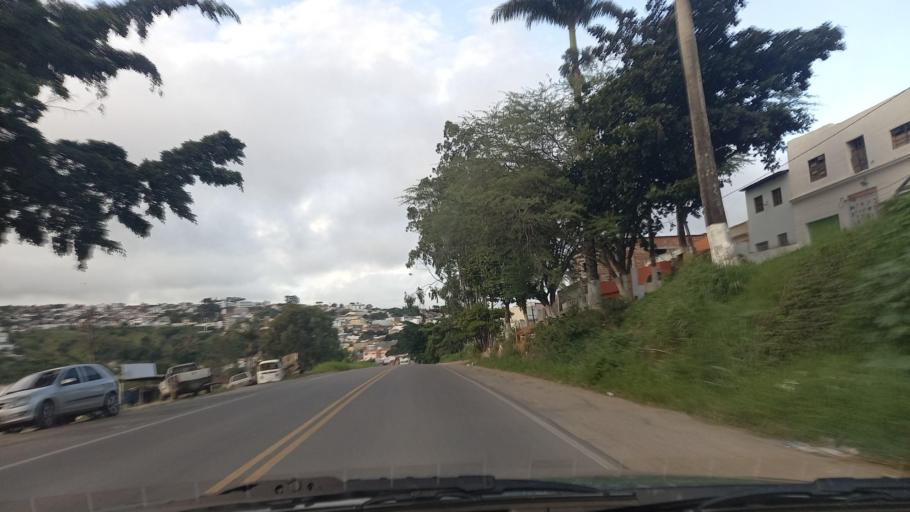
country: BR
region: Pernambuco
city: Garanhuns
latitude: -8.8971
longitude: -36.5021
